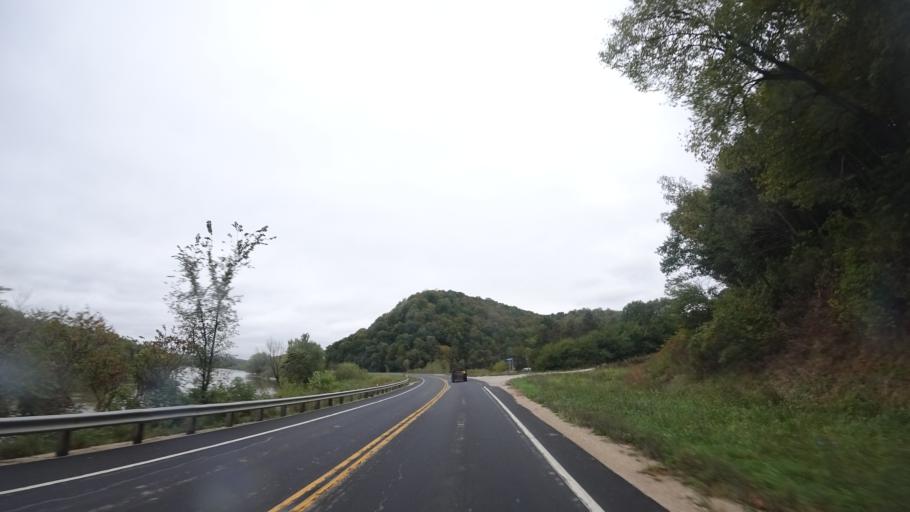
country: US
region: Wisconsin
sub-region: Grant County
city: Boscobel
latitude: 43.1380
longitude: -90.7402
